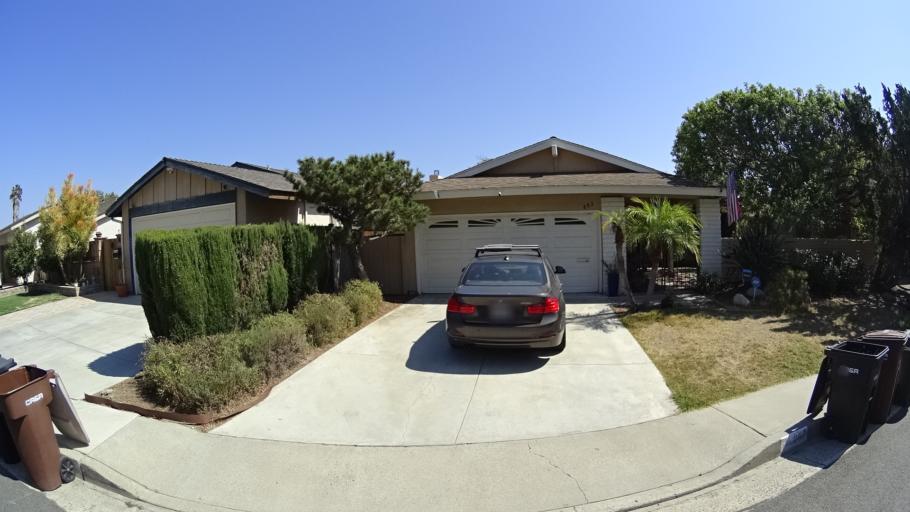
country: US
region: California
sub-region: Orange County
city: San Juan Capistrano
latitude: 33.4608
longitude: -117.6429
